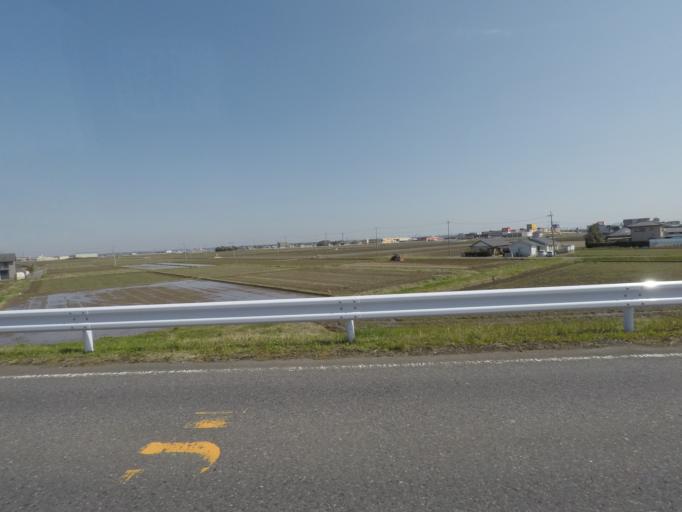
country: JP
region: Chiba
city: Katori-shi
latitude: 35.9147
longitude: 140.4805
